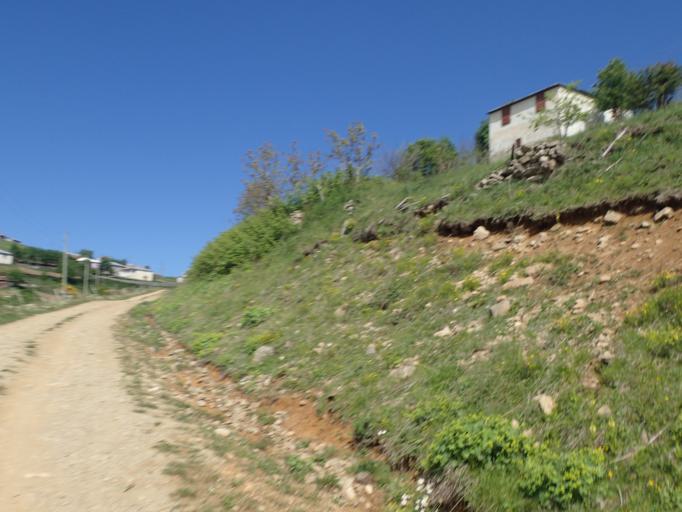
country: TR
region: Ordu
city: Topcam
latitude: 40.6530
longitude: 37.9309
